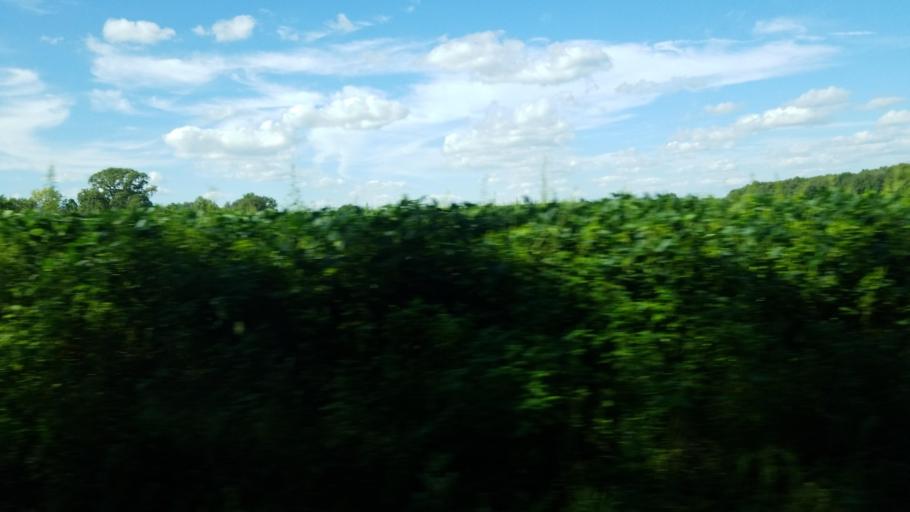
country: US
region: Illinois
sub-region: Saline County
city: Harrisburg
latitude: 37.8127
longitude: -88.5661
